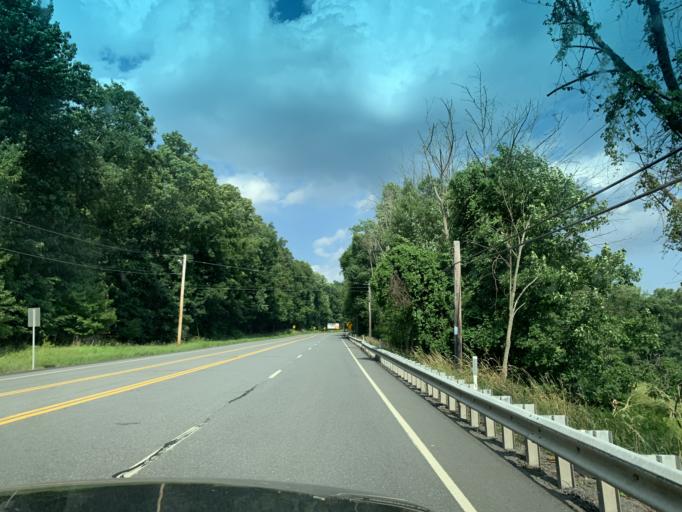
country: US
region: Pennsylvania
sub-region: Schuylkill County
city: Girardville
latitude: 40.7769
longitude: -76.2795
